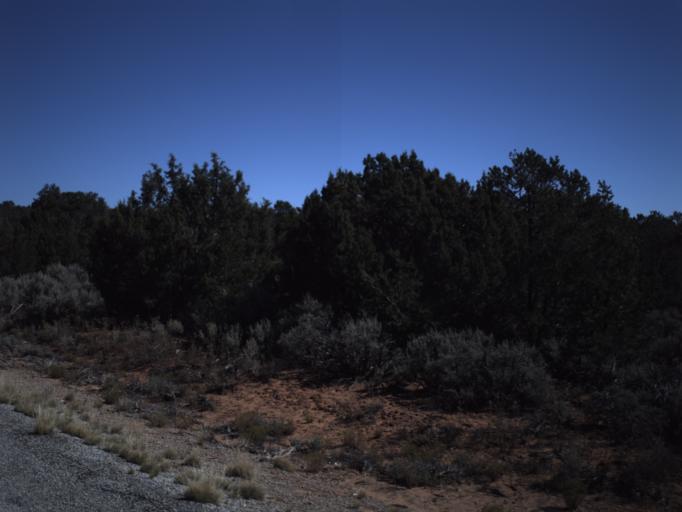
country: US
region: Utah
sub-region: San Juan County
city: Blanding
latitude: 37.5488
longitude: -109.9416
